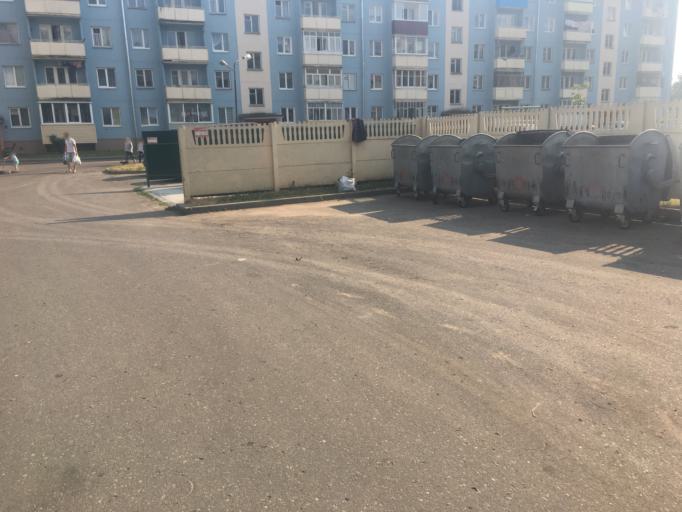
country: BY
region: Grodnenskaya
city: Hrodna
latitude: 53.6668
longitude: 23.8032
